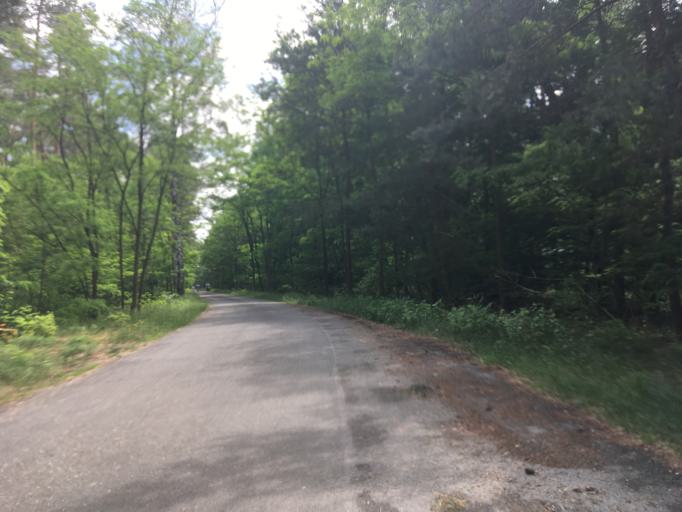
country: DE
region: Berlin
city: Muggelheim
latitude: 52.4042
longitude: 13.6472
